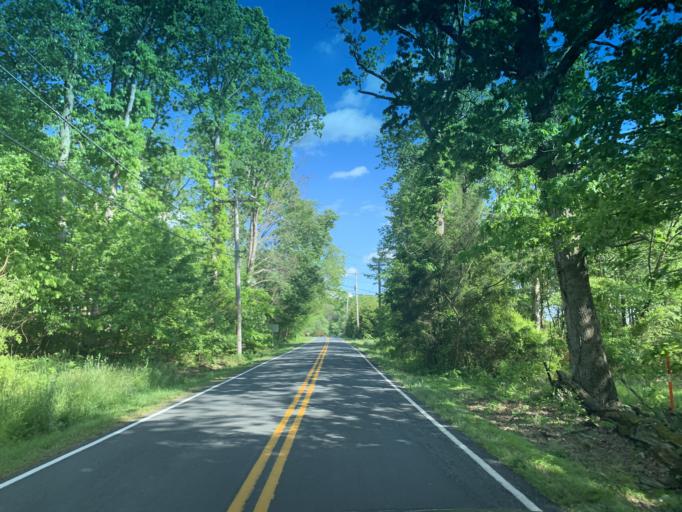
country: US
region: Maryland
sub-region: Cecil County
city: Rising Sun
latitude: 39.7029
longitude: -76.1783
